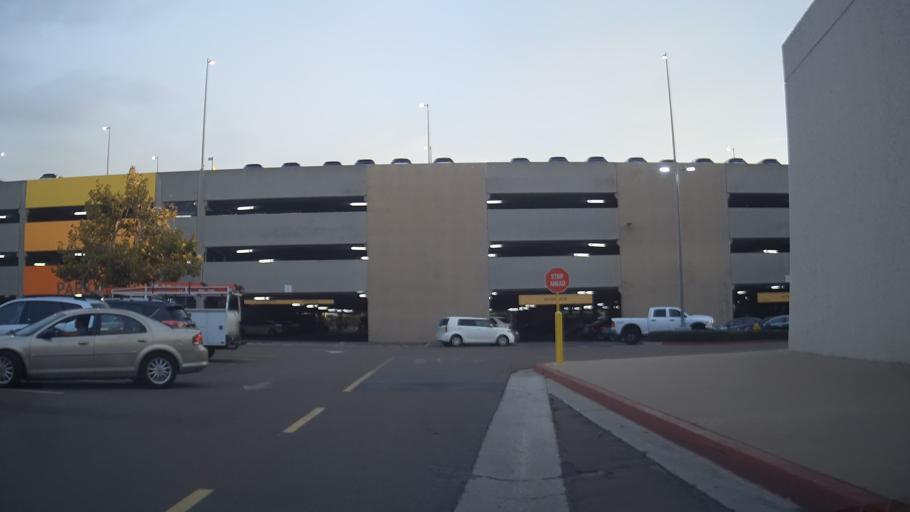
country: US
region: California
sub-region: San Diego County
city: El Cajon
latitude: 32.8055
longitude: -116.9648
